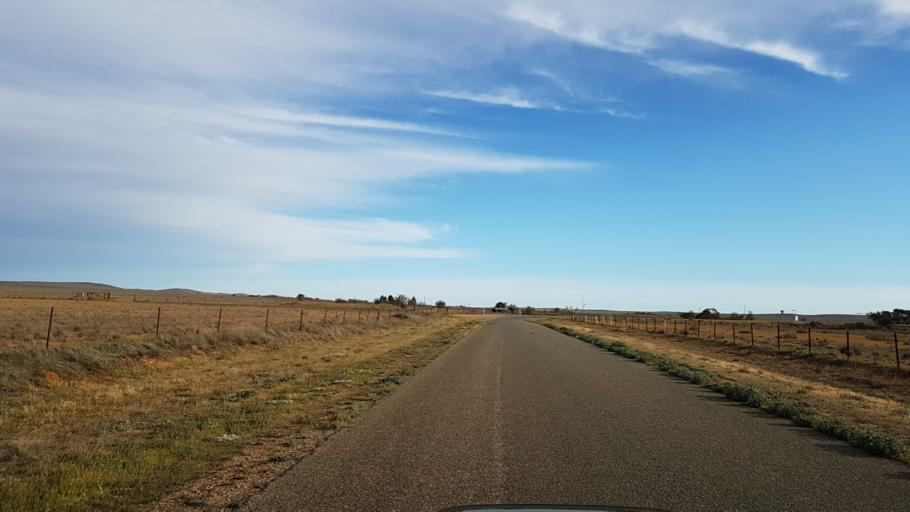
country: AU
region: South Australia
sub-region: Peterborough
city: Peterborough
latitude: -32.9888
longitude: 138.8496
